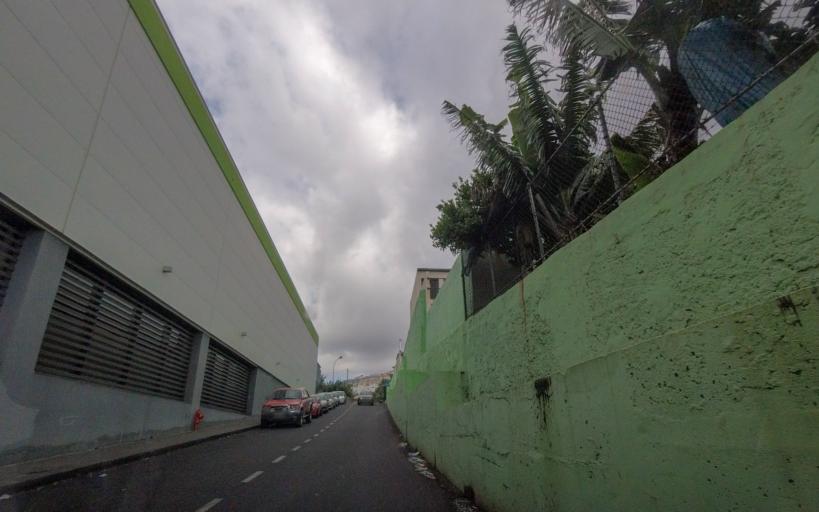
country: PT
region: Madeira
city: Camara de Lobos
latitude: 32.6560
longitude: -16.9462
